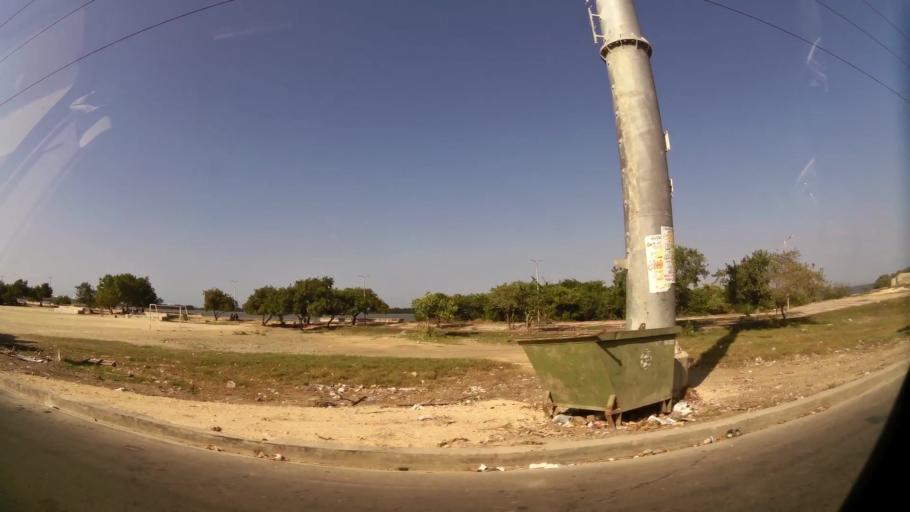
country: CO
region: Bolivar
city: Cartagena
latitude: 10.4154
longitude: -75.5051
